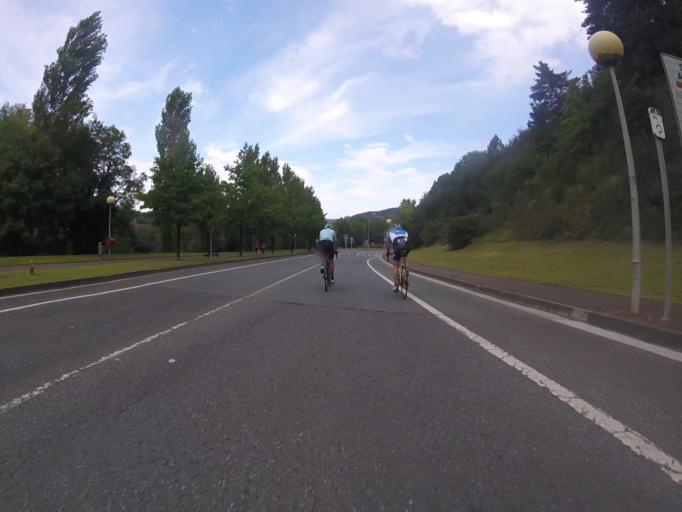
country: ES
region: Basque Country
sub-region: Provincia de Guipuzcoa
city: Villabona
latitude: 43.1925
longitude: -2.0533
